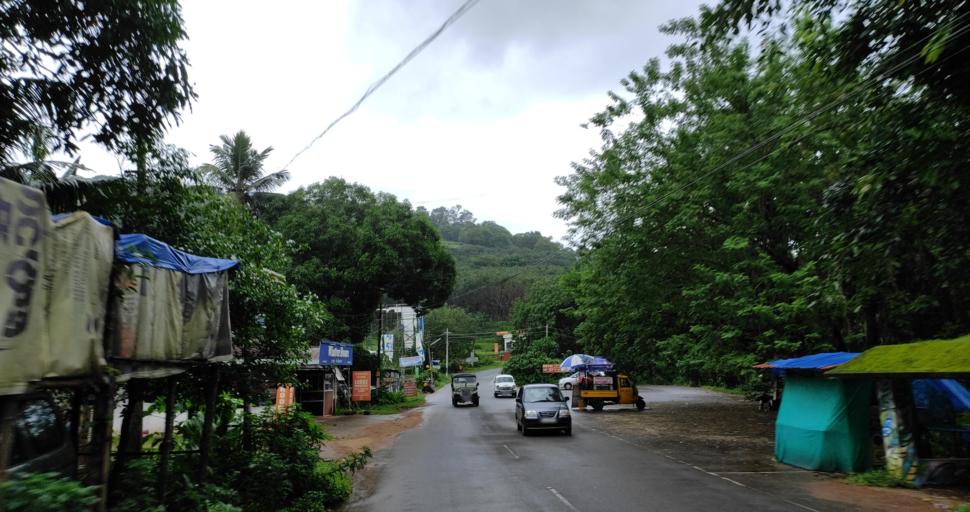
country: IN
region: Kerala
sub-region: Ernakulam
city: Angamali
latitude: 10.2915
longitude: 76.5391
